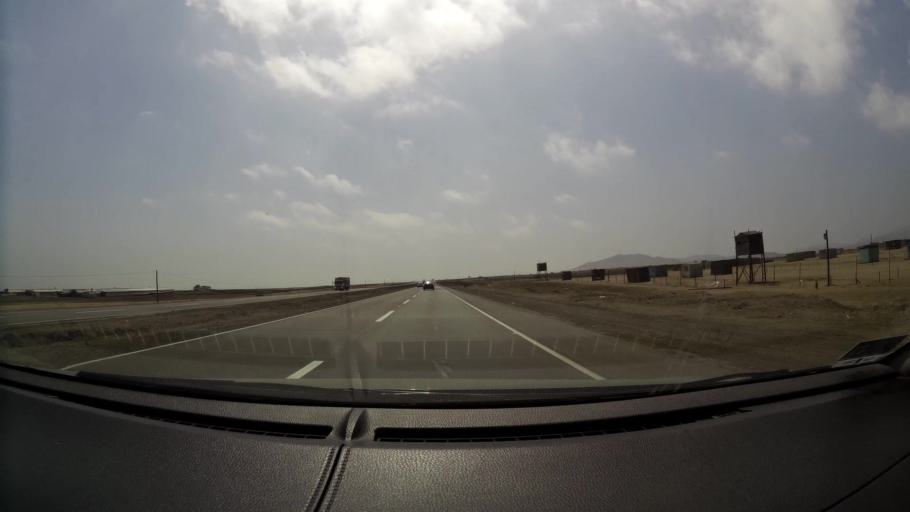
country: PE
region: Lima
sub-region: Provincia de Huaral
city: Huaral
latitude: -11.3703
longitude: -77.4419
